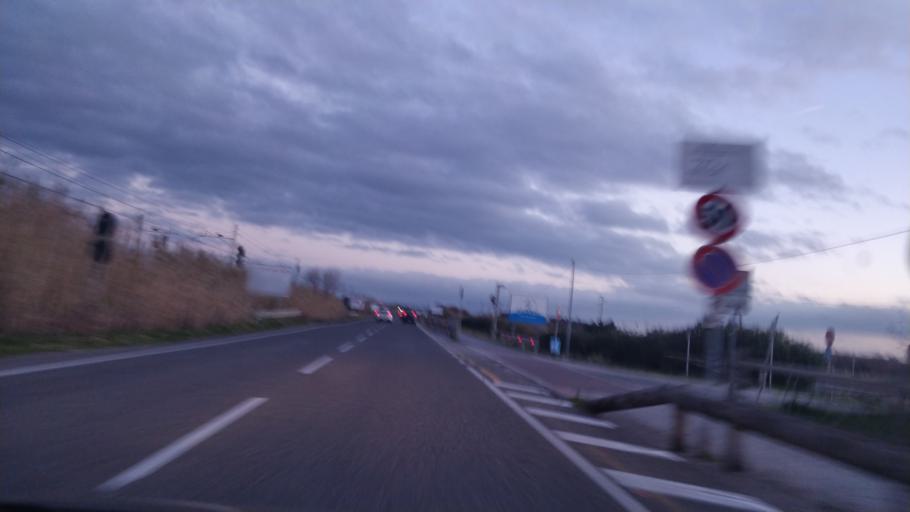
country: IT
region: Tuscany
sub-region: Provincia di Livorno
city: Rosignano Solvay-Castiglioncello
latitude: 43.3765
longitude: 10.4469
